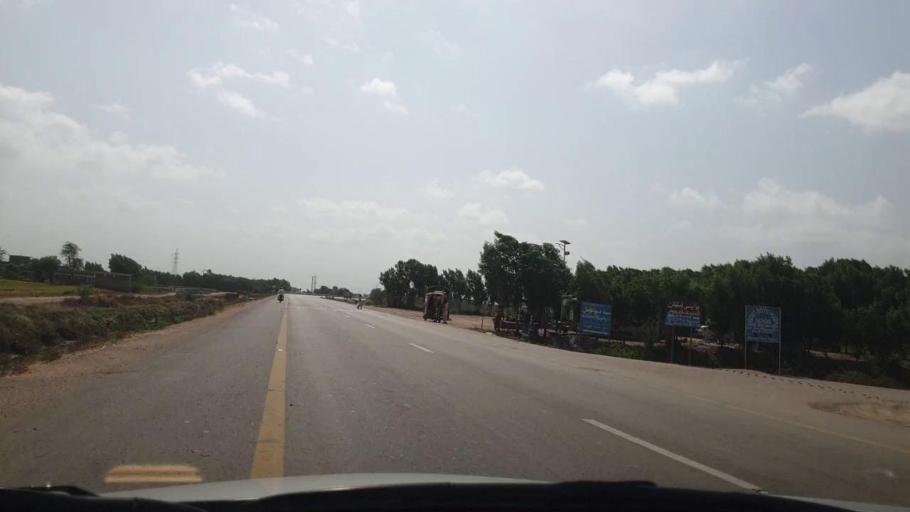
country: PK
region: Sindh
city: Matli
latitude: 24.9716
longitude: 68.6778
